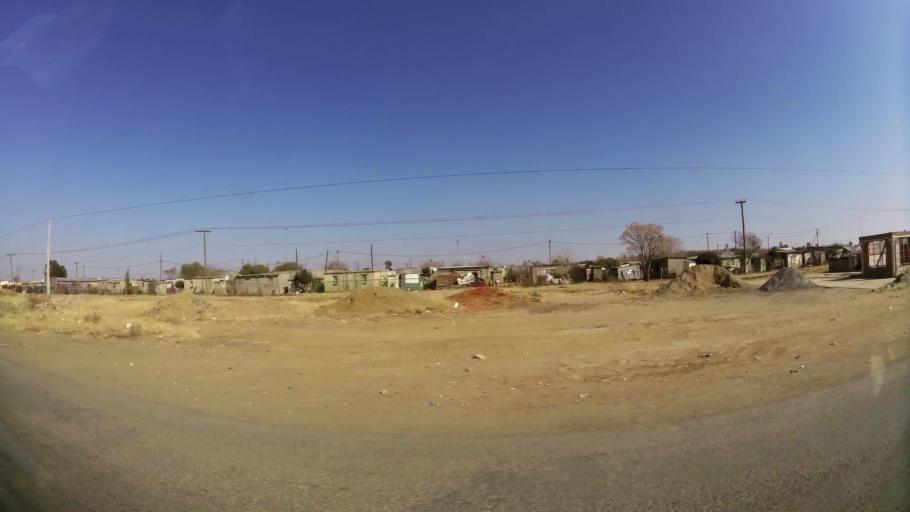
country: ZA
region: Orange Free State
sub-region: Mangaung Metropolitan Municipality
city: Bloemfontein
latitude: -29.1636
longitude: 26.2577
